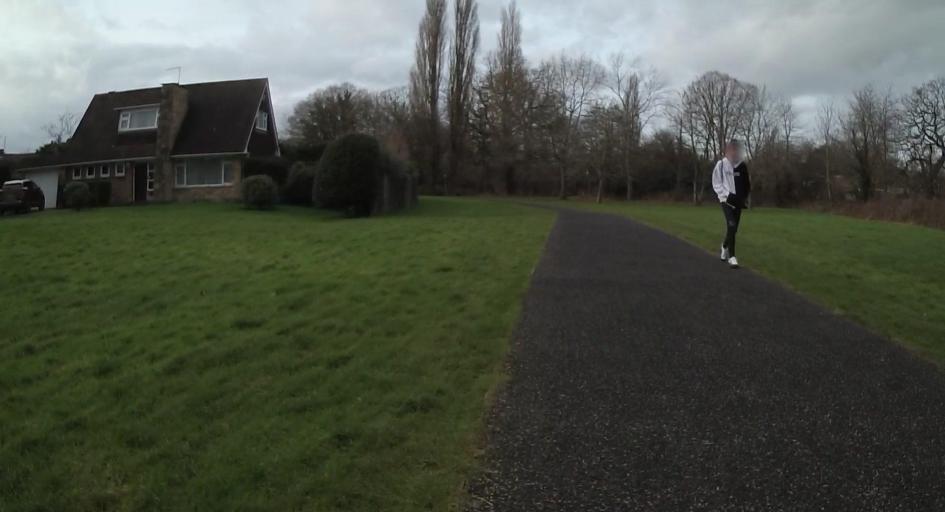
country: GB
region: England
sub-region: Wokingham
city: Wokingham
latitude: 51.4100
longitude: -0.8491
